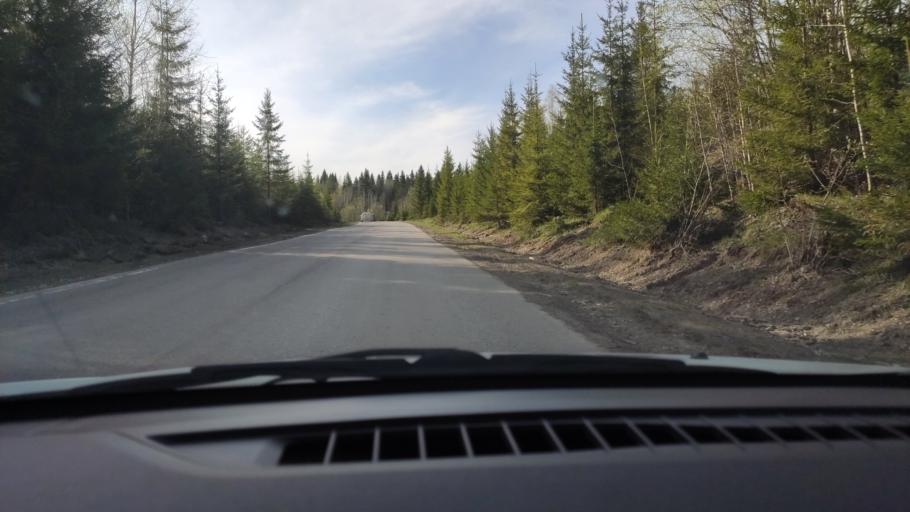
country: RU
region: Perm
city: Novyye Lyady
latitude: 57.9412
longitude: 56.6145
